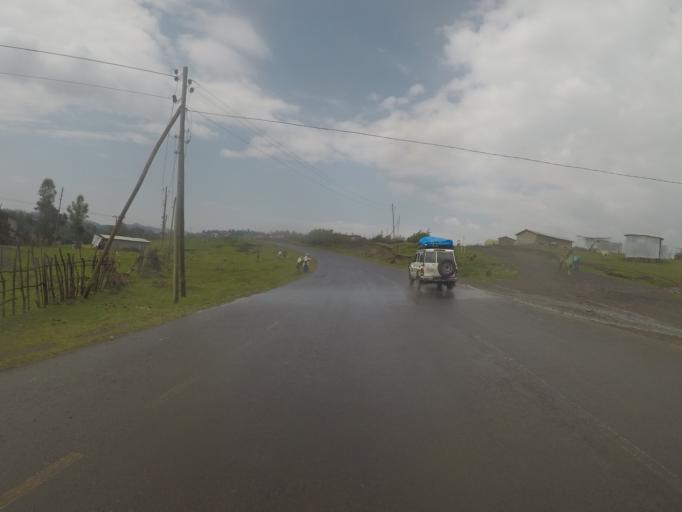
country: ET
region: Amhara
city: Debark'
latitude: 13.1302
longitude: 37.8912
